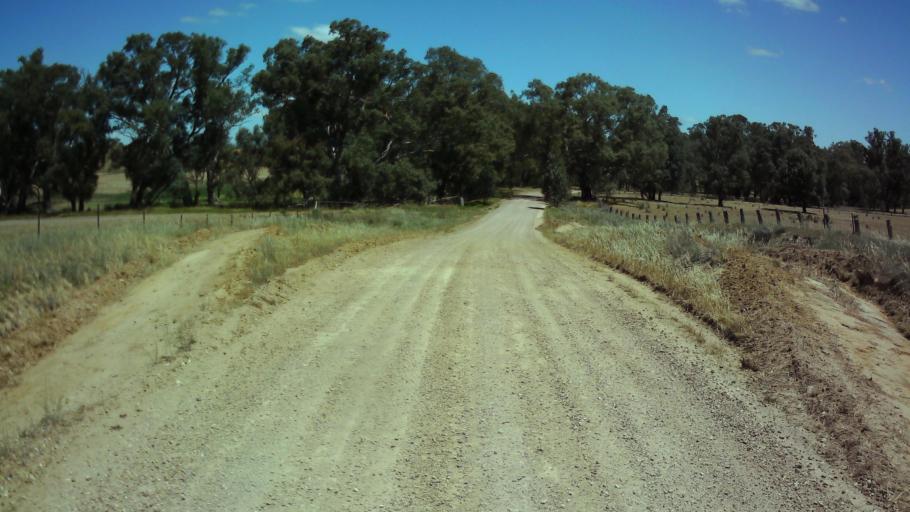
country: AU
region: New South Wales
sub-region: Weddin
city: Grenfell
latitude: -33.9321
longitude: 148.3343
